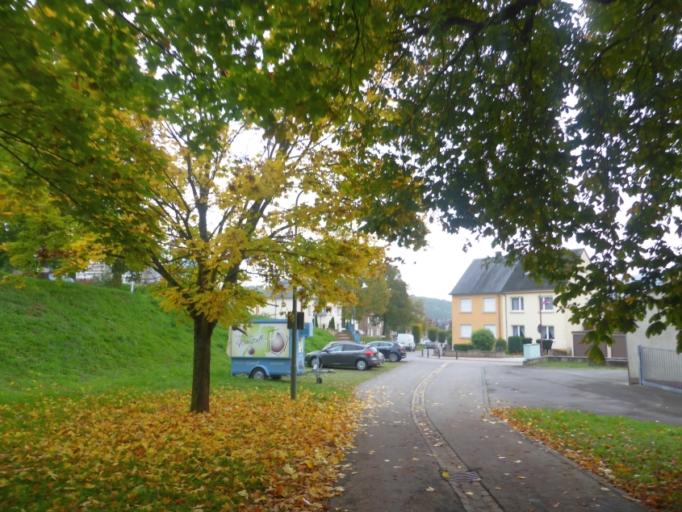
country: DE
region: Rheinland-Pfalz
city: Oberbillig
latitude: 49.7152
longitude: 6.4943
